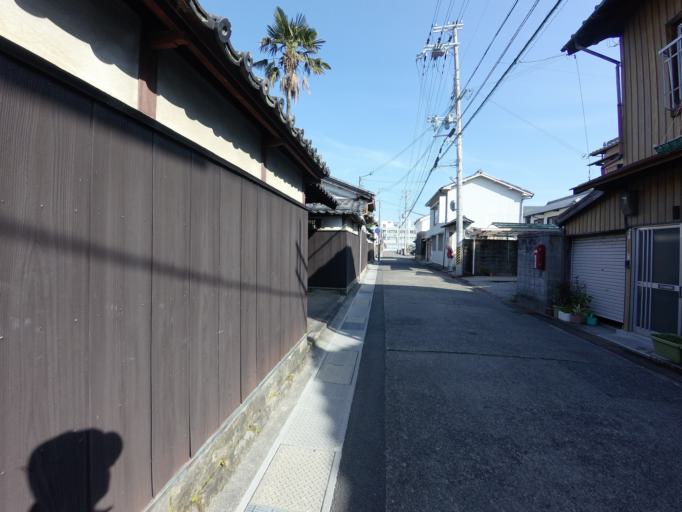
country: JP
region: Wakayama
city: Tanabe
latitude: 33.7302
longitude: 135.3770
